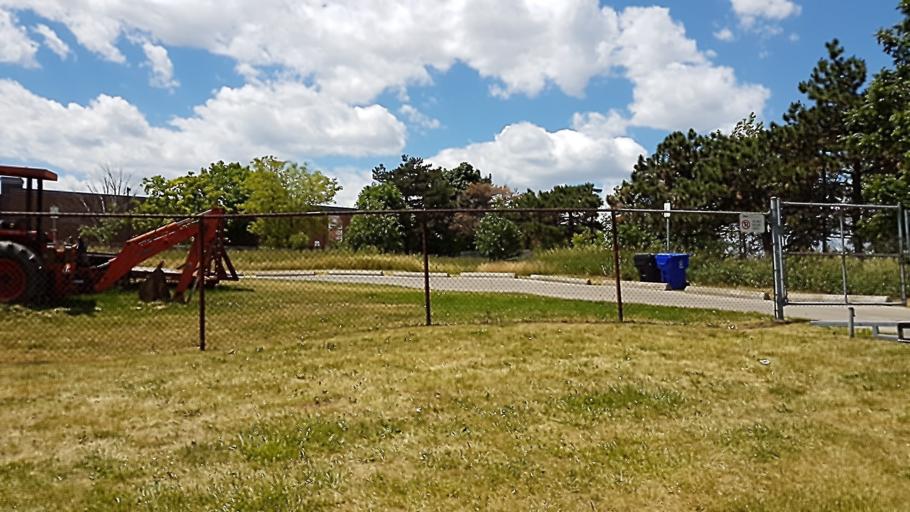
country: CA
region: Ontario
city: Scarborough
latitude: 43.7148
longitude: -79.2390
